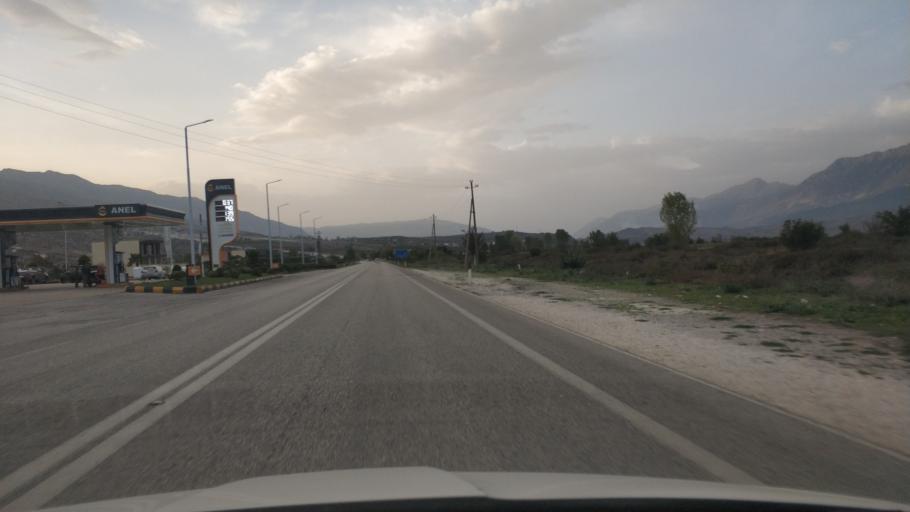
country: AL
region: Gjirokaster
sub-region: Rrethi i Gjirokastres
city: Dervician
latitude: 40.0303
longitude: 20.1854
